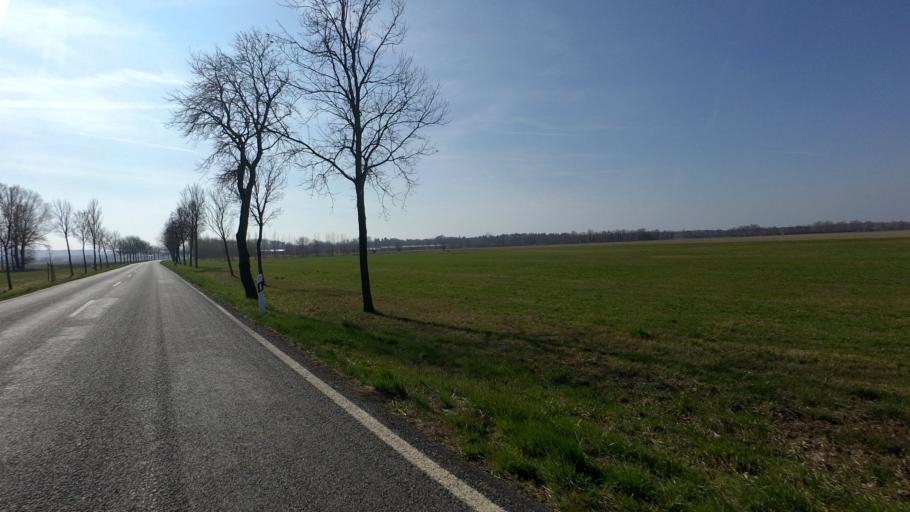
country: DE
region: Brandenburg
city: Sperenberg
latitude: 52.0592
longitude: 13.3246
